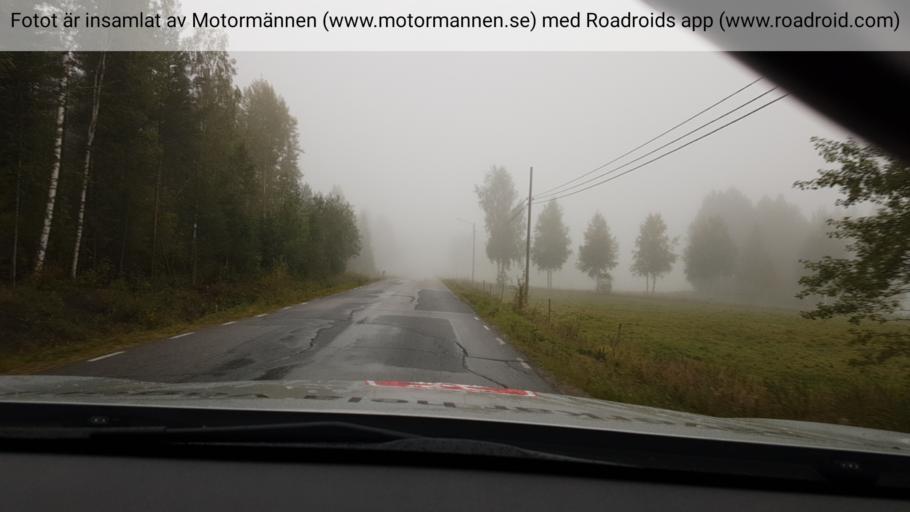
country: SE
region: Vaesterbotten
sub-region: Vannas Kommun
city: Vannasby
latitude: 64.0776
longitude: 20.0567
